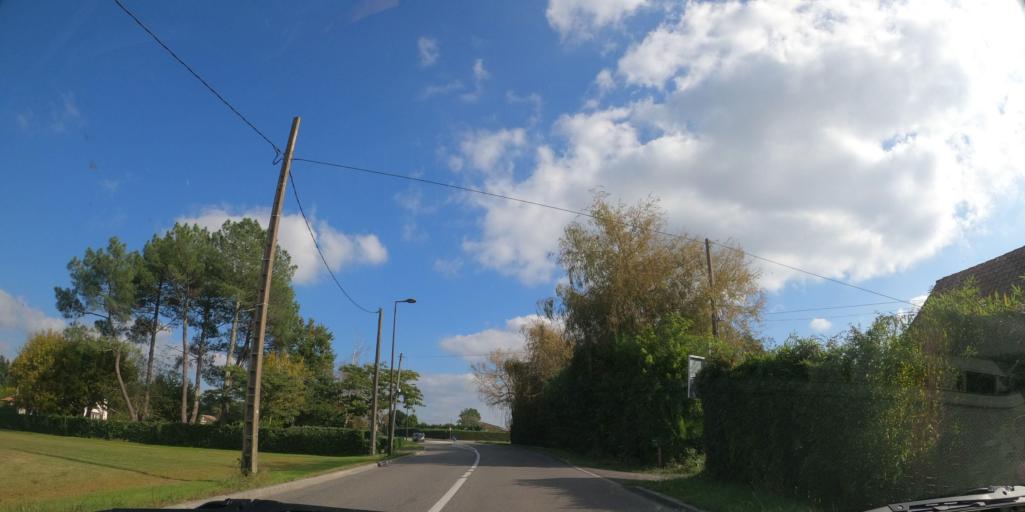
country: FR
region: Aquitaine
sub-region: Departement des Landes
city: Soustons
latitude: 43.7453
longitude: -1.3112
